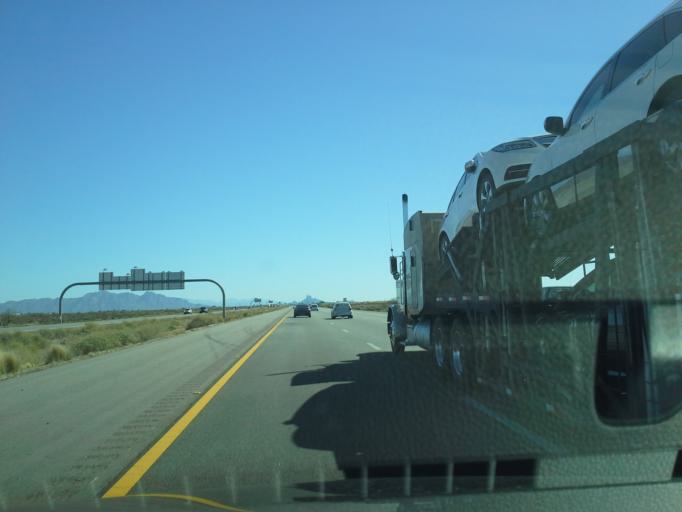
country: US
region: Arizona
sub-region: Pinal County
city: Arizona City
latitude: 32.8032
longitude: -111.6615
